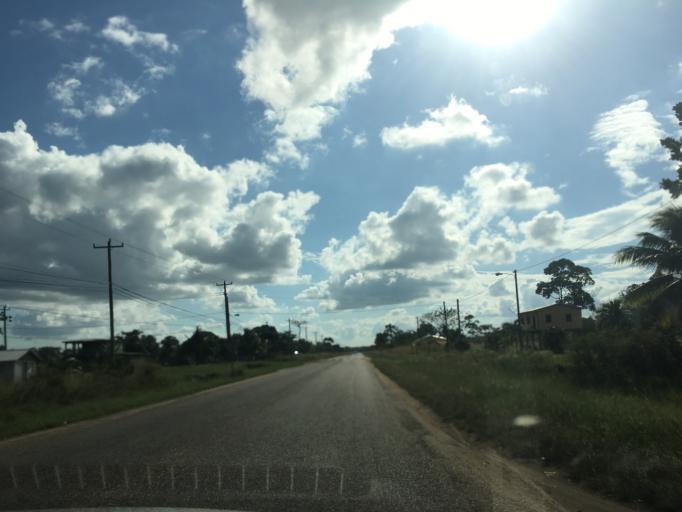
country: BZ
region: Stann Creek
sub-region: Dangriga
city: Dangriga
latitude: 16.8847
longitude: -88.3404
